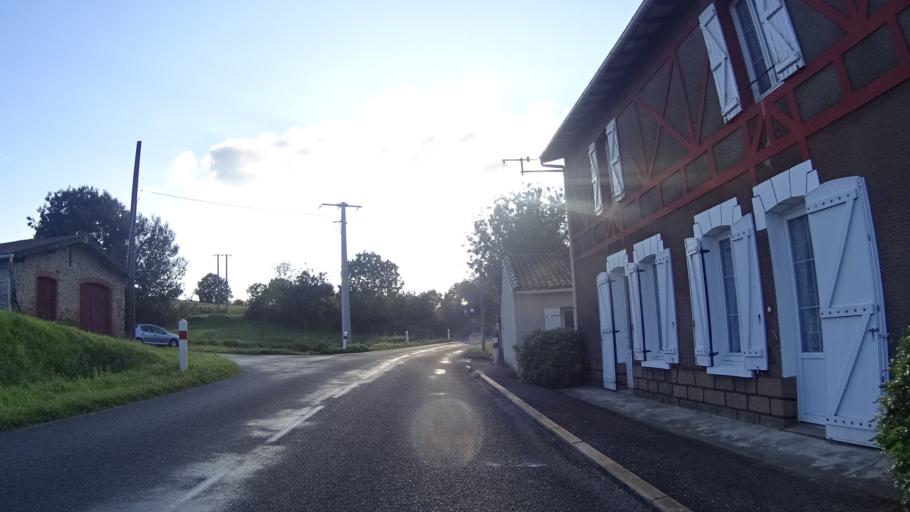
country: FR
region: Pays de la Loire
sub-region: Departement de Maine-et-Loire
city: Drain
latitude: 47.3444
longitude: -1.1998
